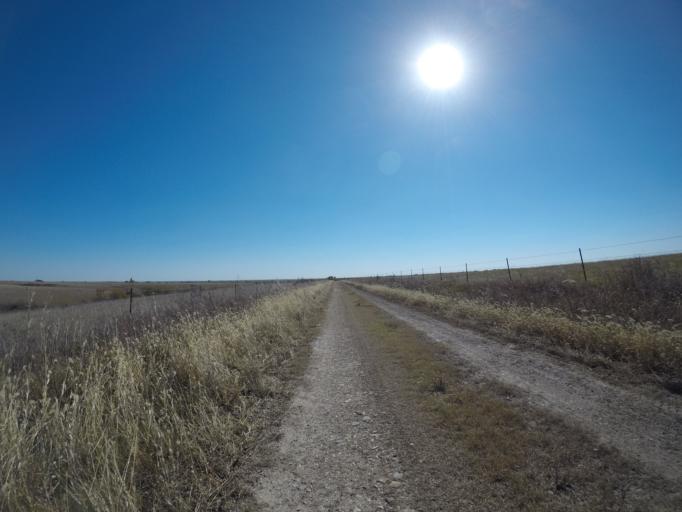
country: US
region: Kansas
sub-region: Wabaunsee County
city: Alma
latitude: 38.9888
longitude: -96.4642
